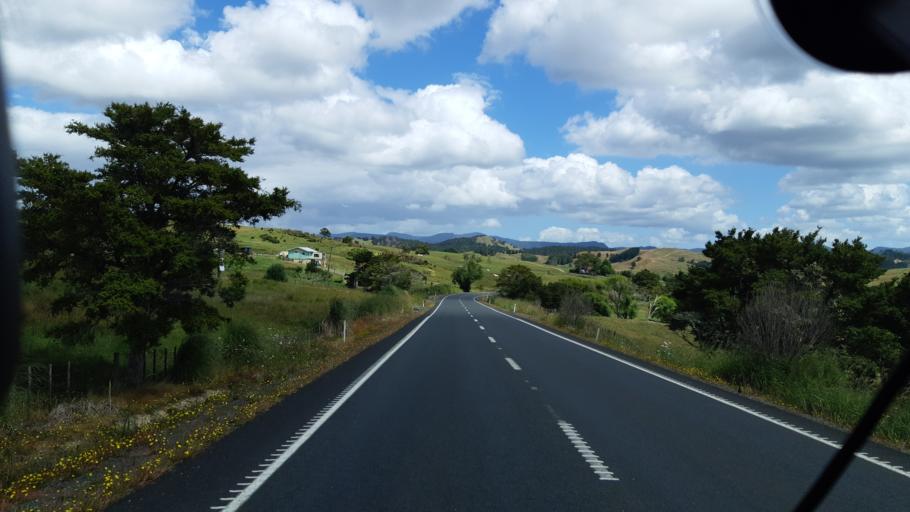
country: NZ
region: Northland
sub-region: Far North District
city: Waimate North
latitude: -35.2950
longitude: 173.5818
